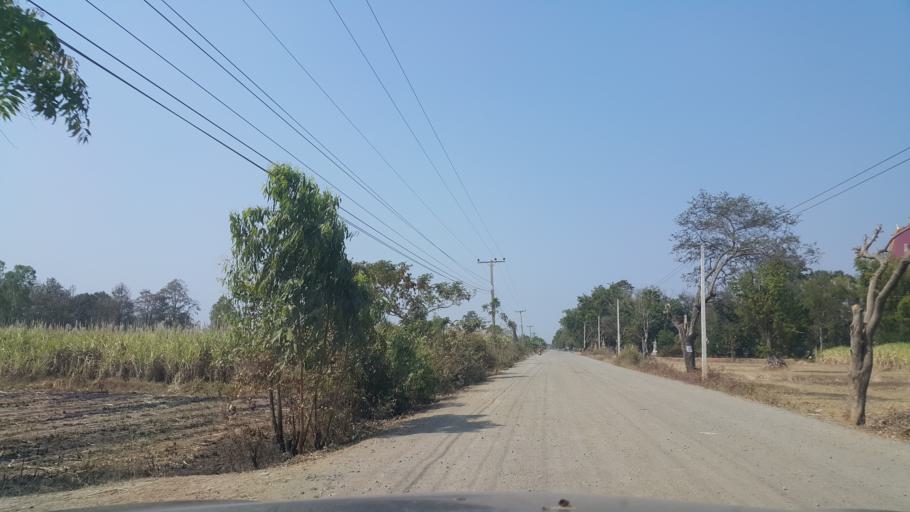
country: TH
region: Buriram
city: Satuek
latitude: 15.1326
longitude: 103.3530
